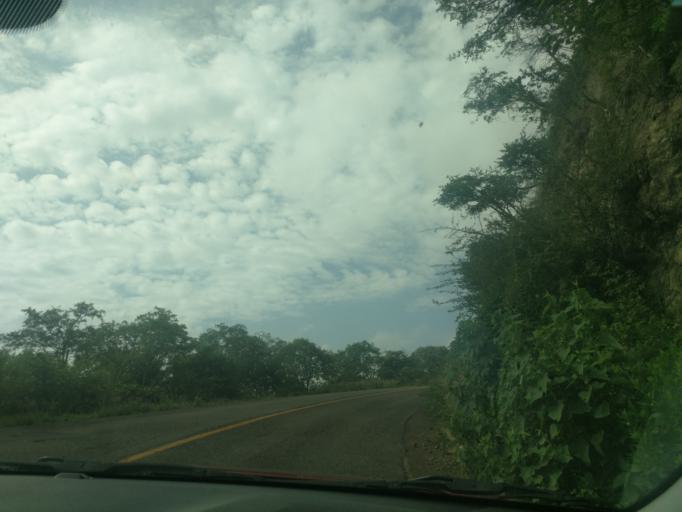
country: MX
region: Jalisco
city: El Salto
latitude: 20.3637
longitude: -104.5836
